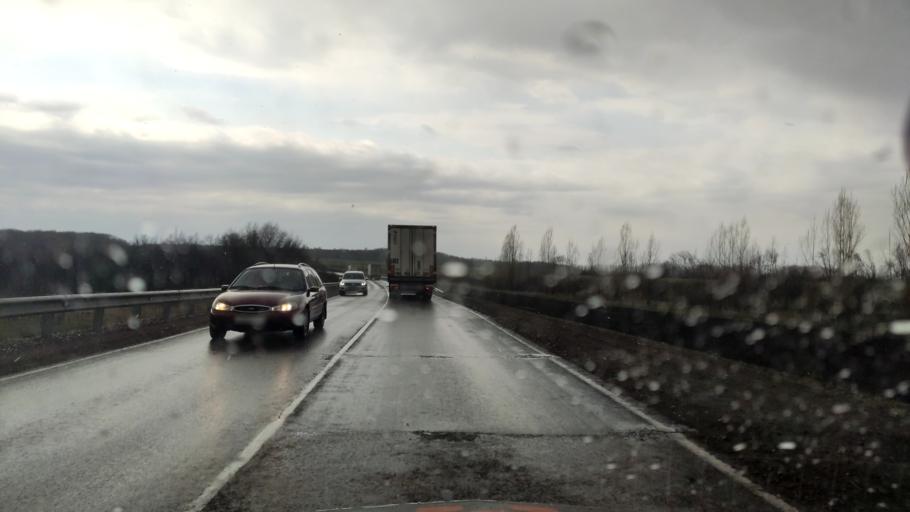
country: RU
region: Voronezj
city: Nizhnedevitsk
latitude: 51.5764
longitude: 38.3189
